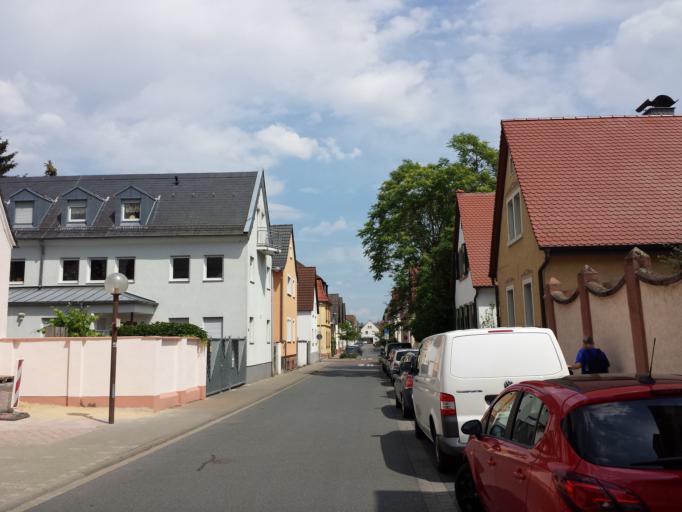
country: DE
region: Hesse
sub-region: Regierungsbezirk Darmstadt
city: Russelsheim
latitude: 49.9961
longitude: 8.4194
